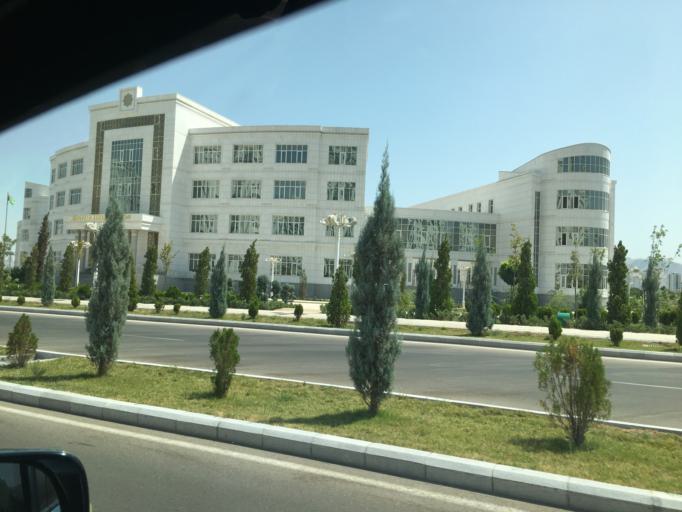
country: TM
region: Ahal
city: Ashgabat
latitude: 37.9144
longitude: 58.3597
